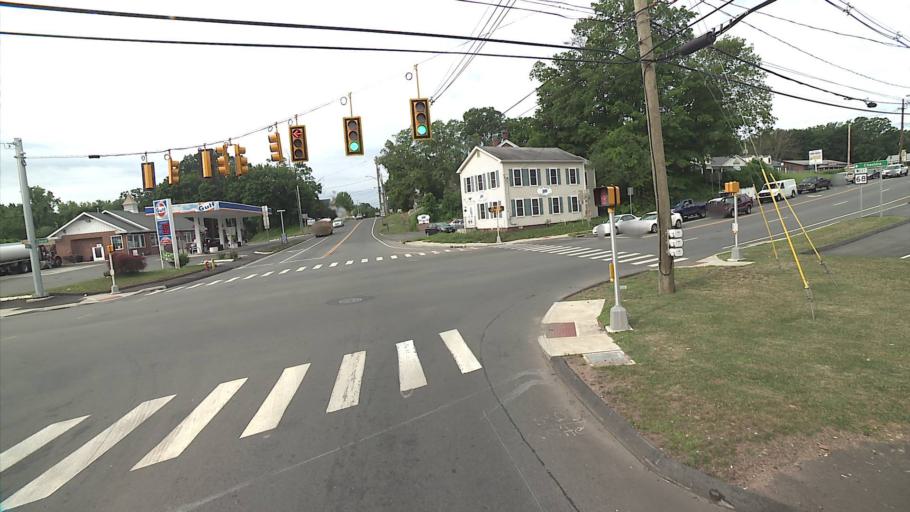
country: US
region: Connecticut
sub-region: New Haven County
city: Wallingford
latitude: 41.4914
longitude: -72.8182
